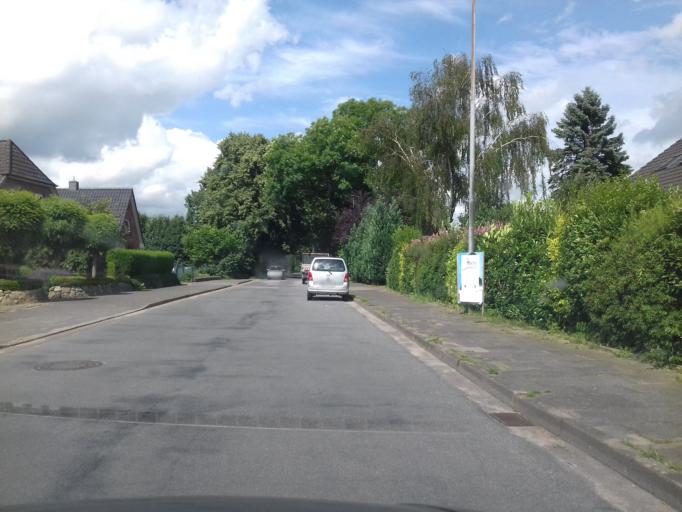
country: DE
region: Schleswig-Holstein
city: Bargteheide
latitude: 53.7381
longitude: 10.2650
